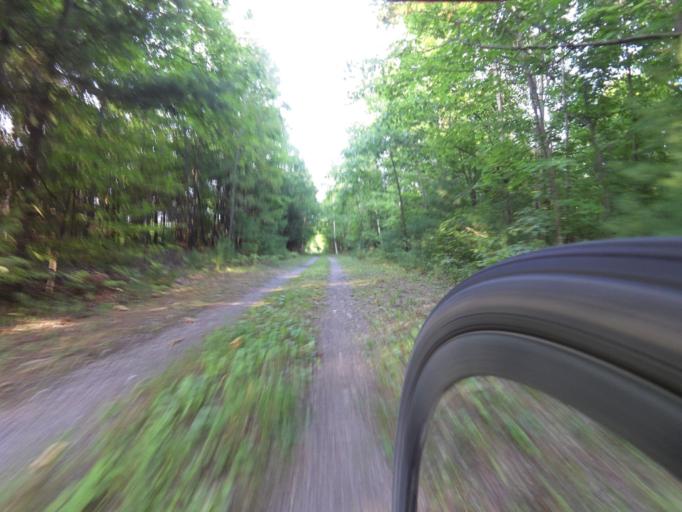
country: CA
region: Ontario
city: Gananoque
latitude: 44.5716
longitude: -76.3456
